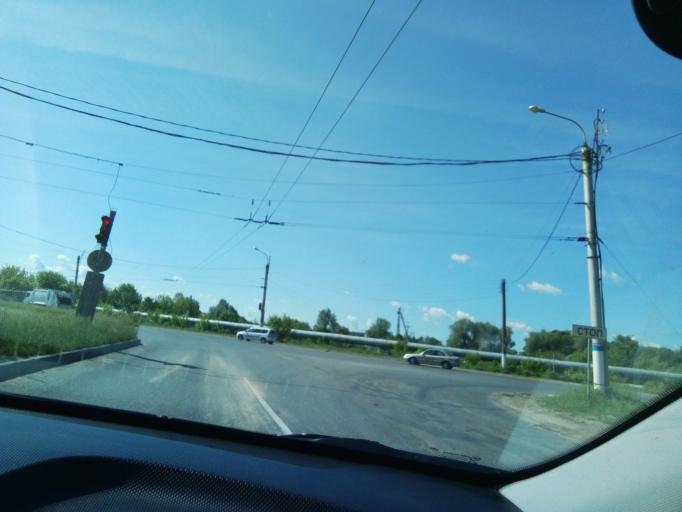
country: RU
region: Chuvashia
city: Novocheboksarsk
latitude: 56.0950
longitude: 47.4943
